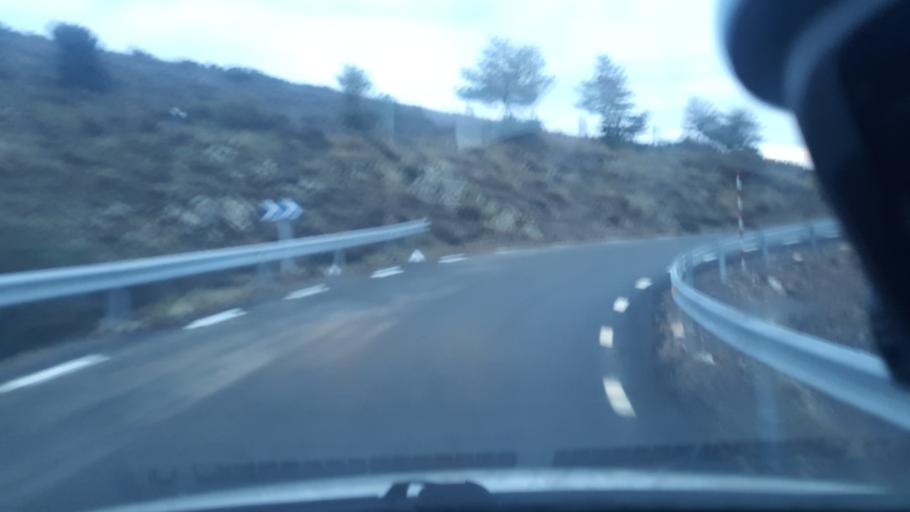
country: ES
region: Castille and Leon
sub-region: Provincia de Avila
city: Ojos-Albos
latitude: 40.7219
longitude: -4.4547
